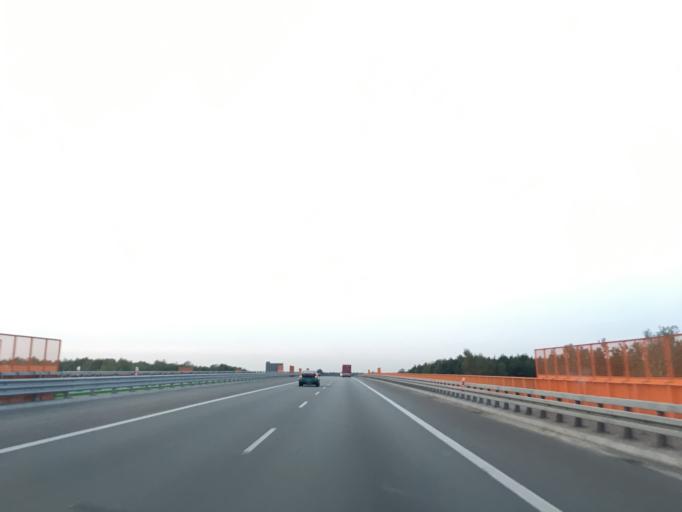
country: PL
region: Lodz Voivodeship
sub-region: Powiat lodzki wschodni
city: Andrespol
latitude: 51.7330
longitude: 19.6032
